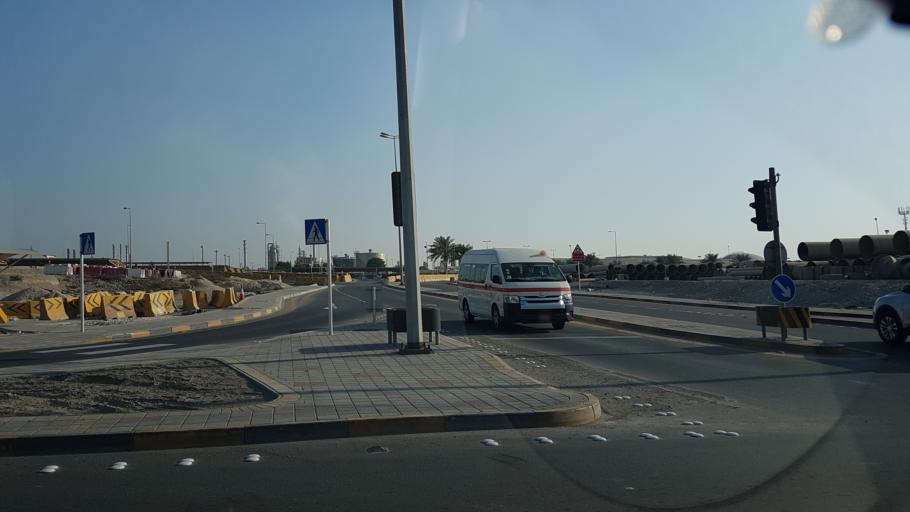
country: BH
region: Northern
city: Sitrah
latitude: 26.1234
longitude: 50.6006
